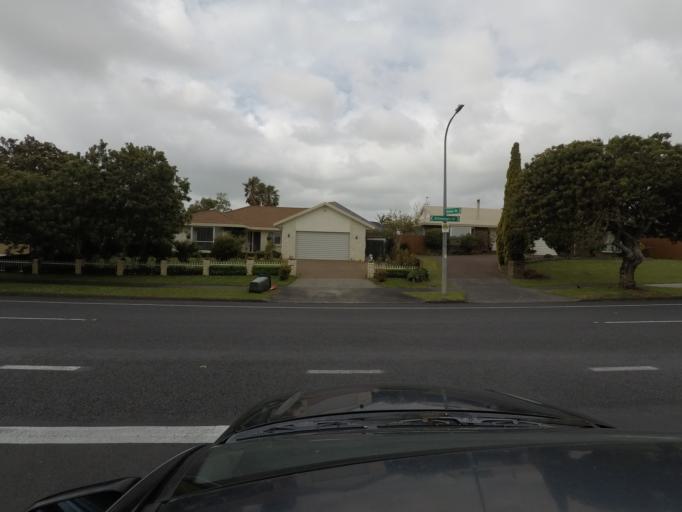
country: NZ
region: Auckland
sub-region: Auckland
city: Pakuranga
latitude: -36.9225
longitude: 174.9201
